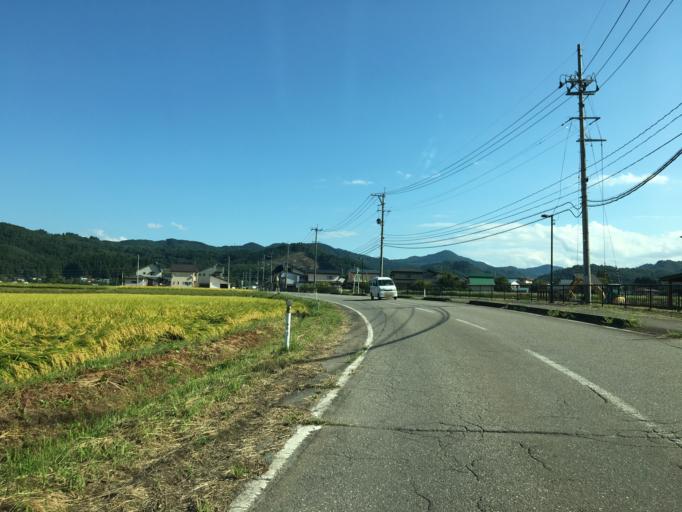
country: JP
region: Fukushima
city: Kitakata
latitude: 37.5922
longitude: 139.6561
